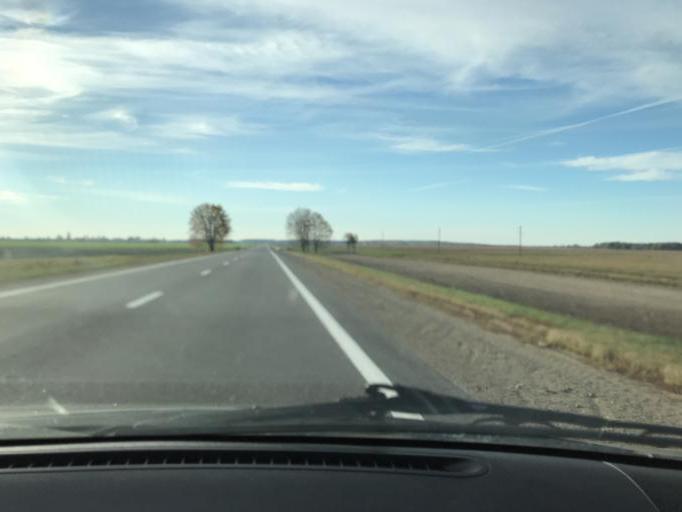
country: BY
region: Brest
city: Ivanava
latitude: 52.1560
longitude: 25.6686
